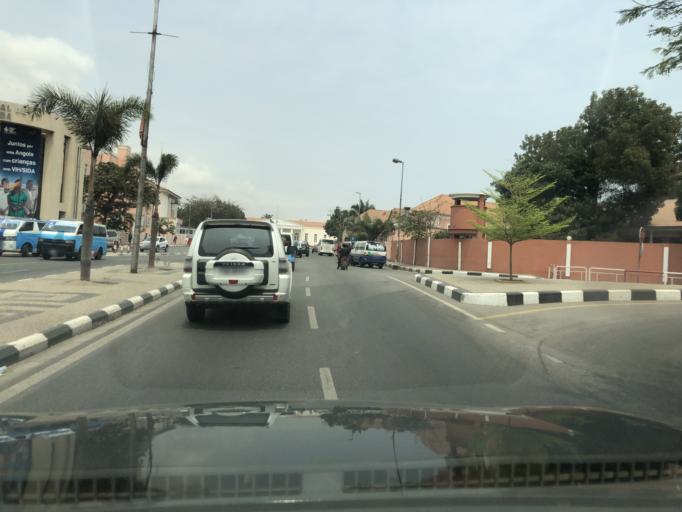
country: AO
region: Luanda
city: Luanda
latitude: -8.8217
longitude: 13.2275
